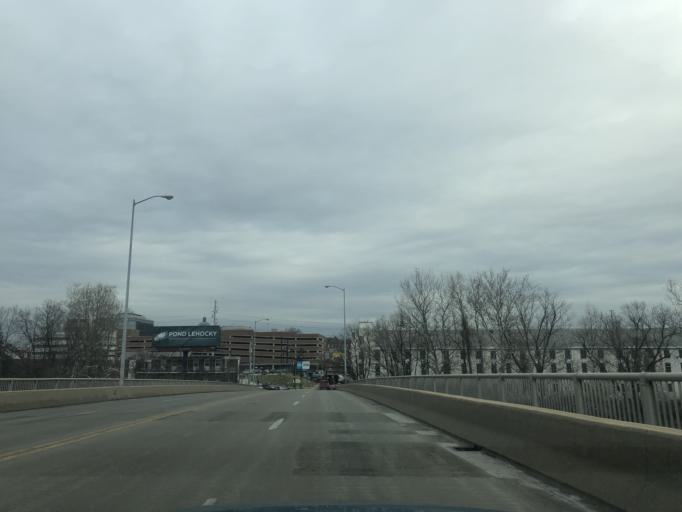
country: US
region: Pennsylvania
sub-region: Montgomery County
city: Bridgeport
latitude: 40.1102
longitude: -75.3443
